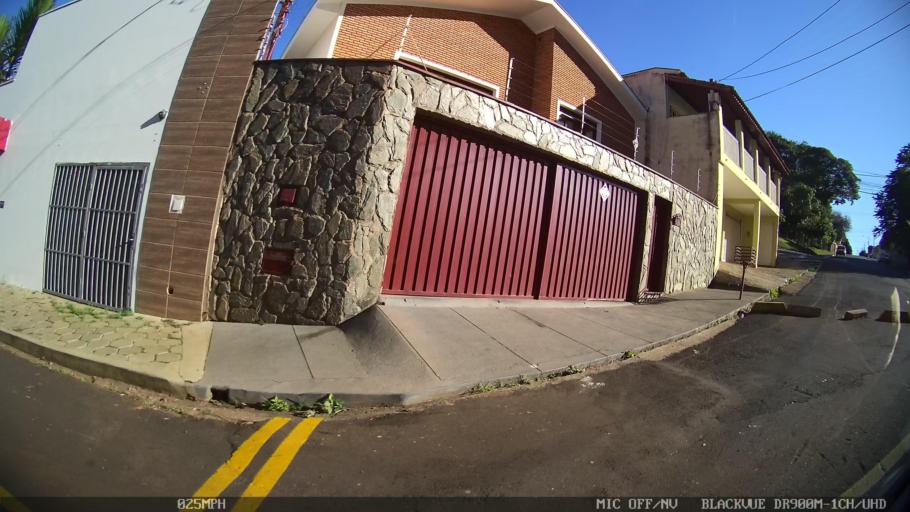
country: BR
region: Sao Paulo
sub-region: Franca
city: Franca
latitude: -20.5500
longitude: -47.4050
